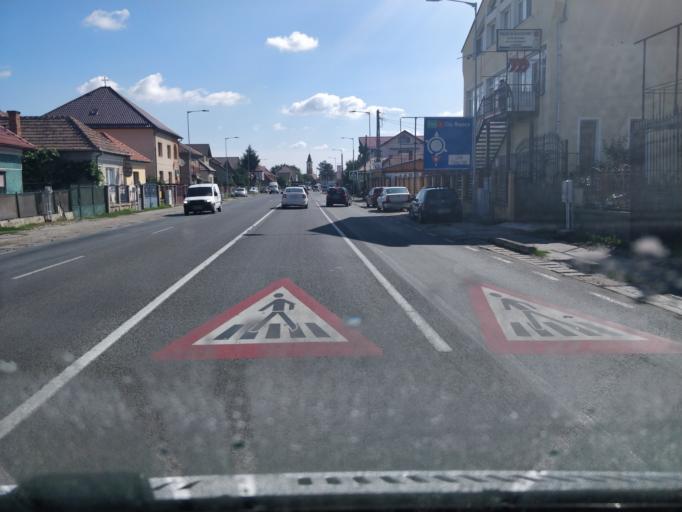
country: RO
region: Cluj
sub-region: Comuna Floresti
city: Floresti
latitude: 46.7441
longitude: 23.4811
